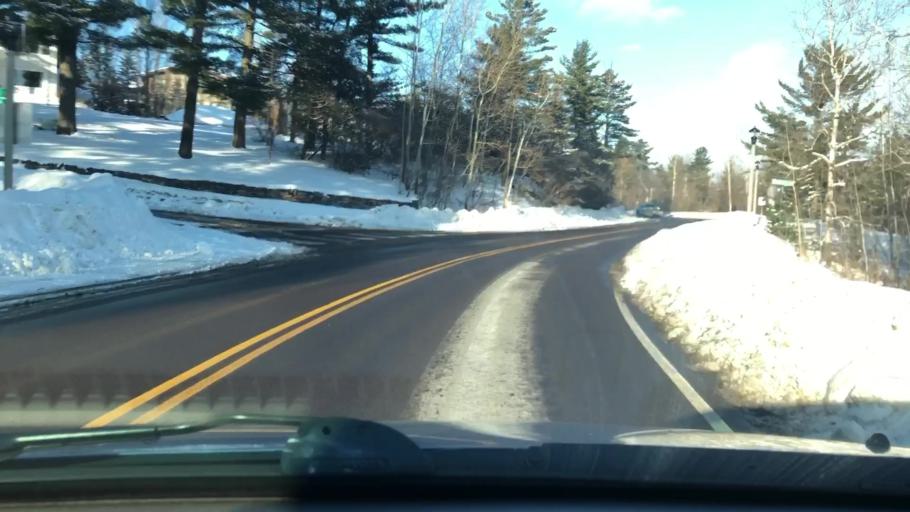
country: US
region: Minnesota
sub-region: Saint Louis County
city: Duluth
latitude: 46.8193
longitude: -92.0705
